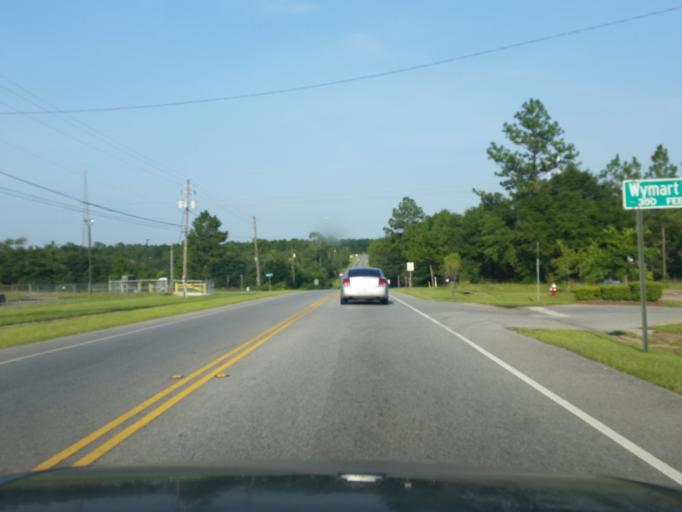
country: US
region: Florida
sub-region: Escambia County
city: Bellview
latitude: 30.4863
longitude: -87.2908
